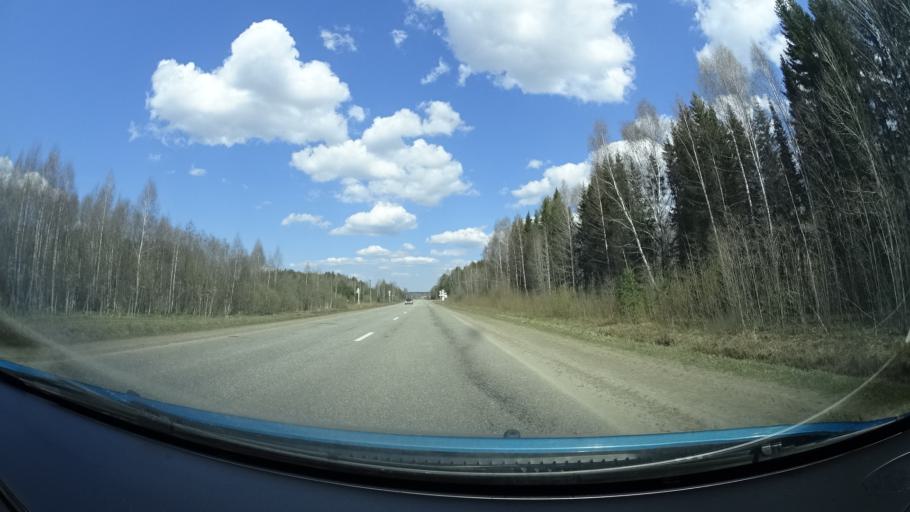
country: RU
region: Perm
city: Osa
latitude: 57.3545
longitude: 55.5984
